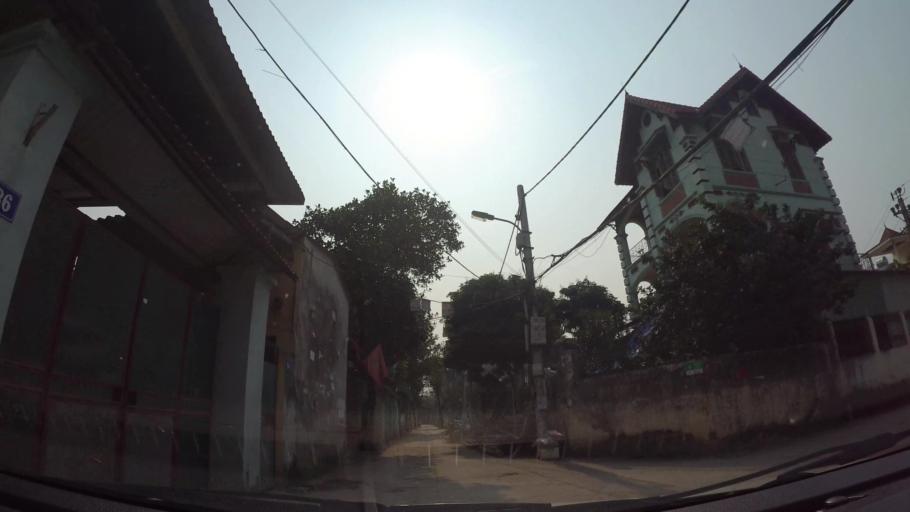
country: VN
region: Ha Noi
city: Ha Dong
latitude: 20.9980
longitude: 105.7530
